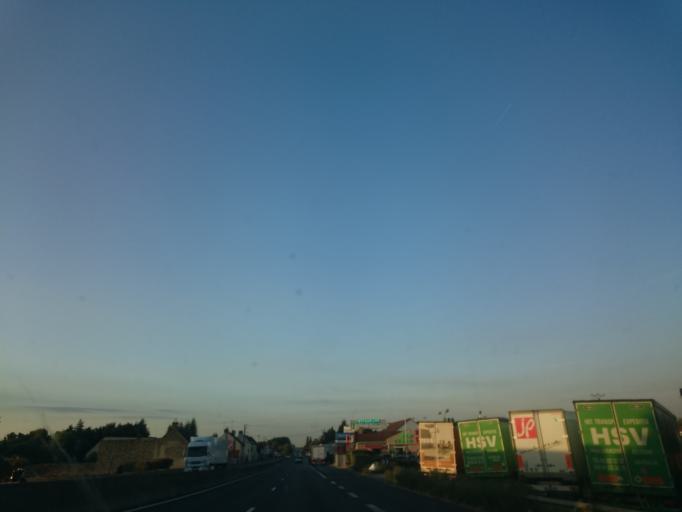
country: FR
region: Ile-de-France
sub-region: Departement de l'Essonne
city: Boissy-sous-Saint-Yon
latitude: 48.5441
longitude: 2.2136
